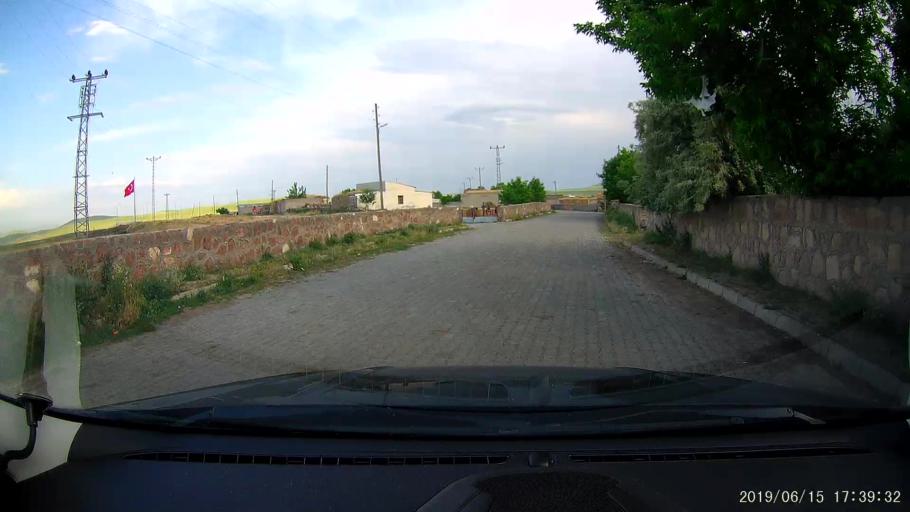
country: TR
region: Kars
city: Basgedikler
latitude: 40.5156
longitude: 43.5706
